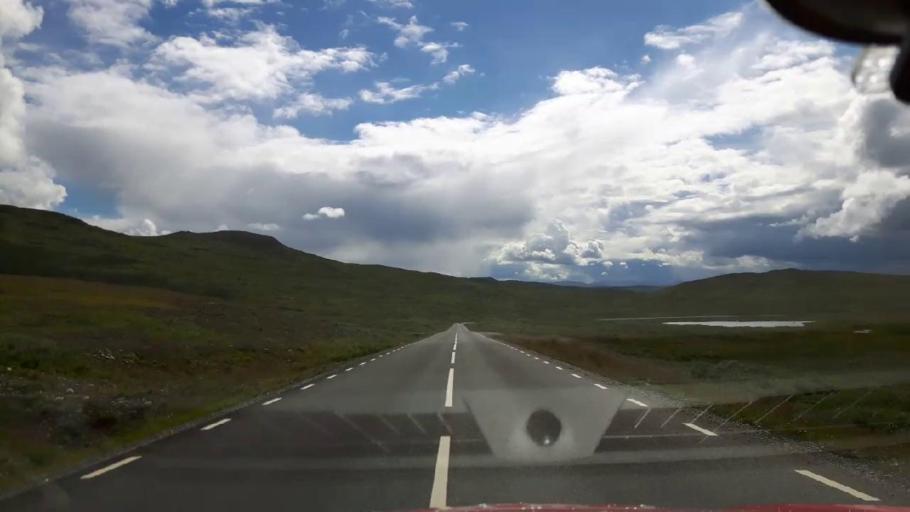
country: NO
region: Nordland
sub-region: Hattfjelldal
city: Hattfjelldal
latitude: 65.0361
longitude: 14.3296
